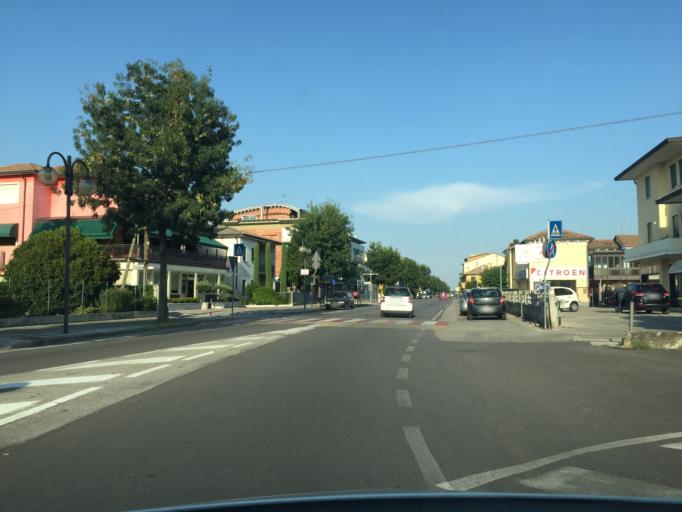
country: IT
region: Veneto
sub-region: Provincia di Padova
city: Cittadella
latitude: 45.6499
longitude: 11.7922
